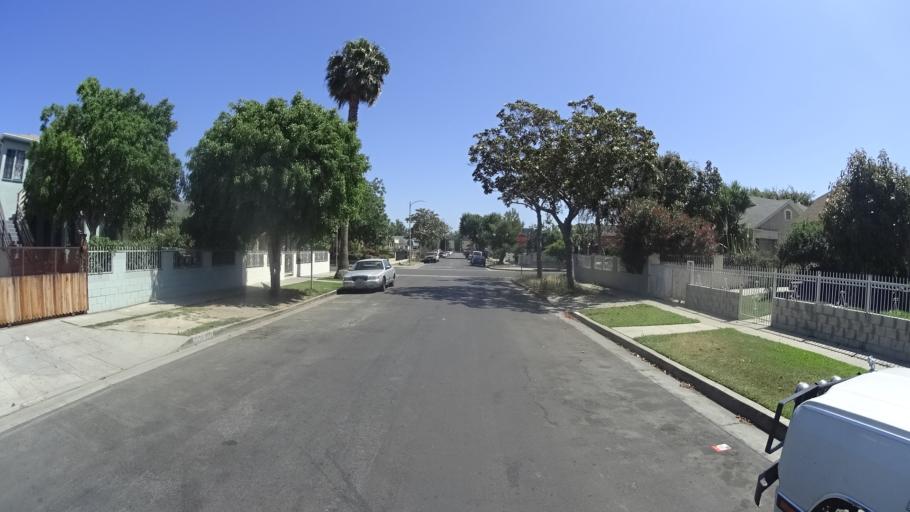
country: US
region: California
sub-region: Los Angeles County
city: View Park-Windsor Hills
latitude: 34.0059
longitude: -118.2970
